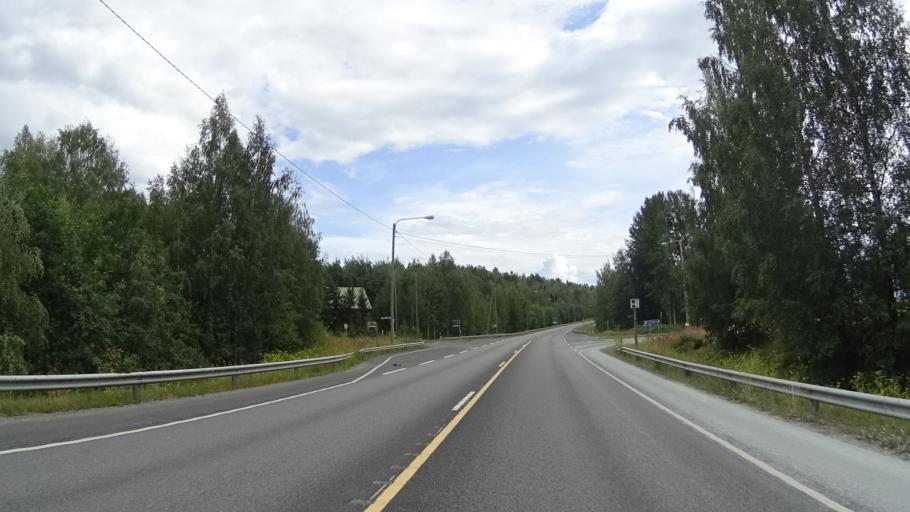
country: FI
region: Pirkanmaa
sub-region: Tampere
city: Kangasala
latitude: 61.4411
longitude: 24.1199
